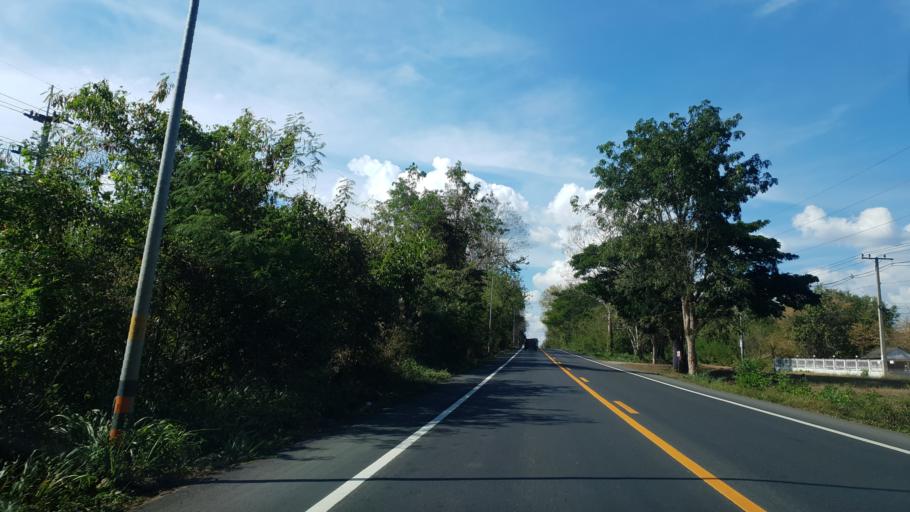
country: TH
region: Phrae
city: Den Chai
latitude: 17.9716
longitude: 100.0446
